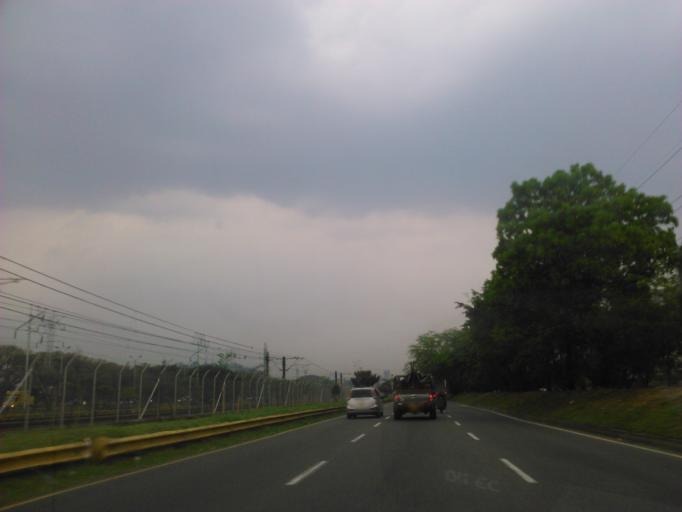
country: CO
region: Antioquia
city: Medellin
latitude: 6.2193
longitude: -75.5770
